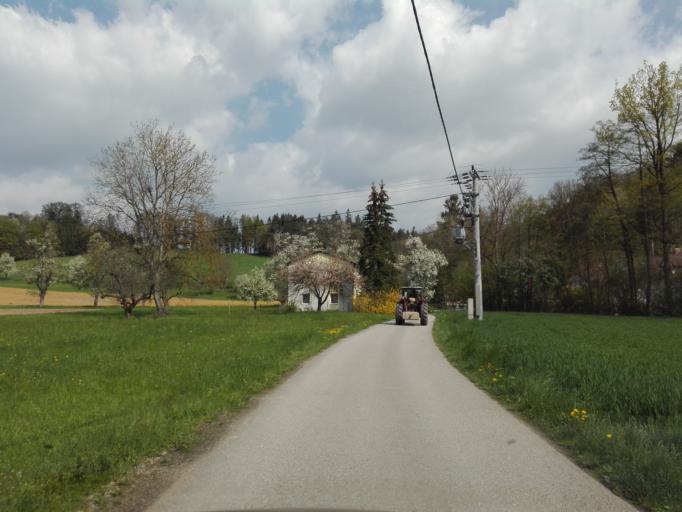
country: AT
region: Upper Austria
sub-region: Politischer Bezirk Perg
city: Perg
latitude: 48.2364
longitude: 14.6872
